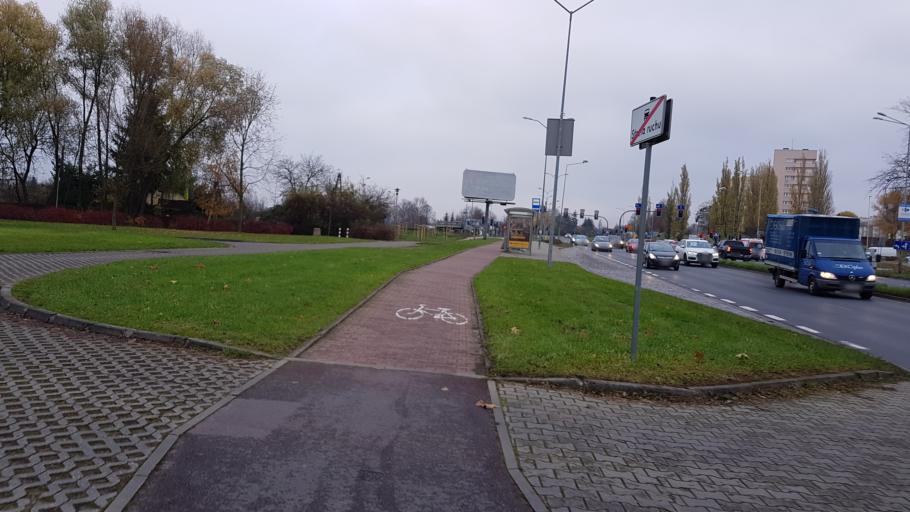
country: PL
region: West Pomeranian Voivodeship
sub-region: Szczecin
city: Szczecin
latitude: 53.4276
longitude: 14.4994
